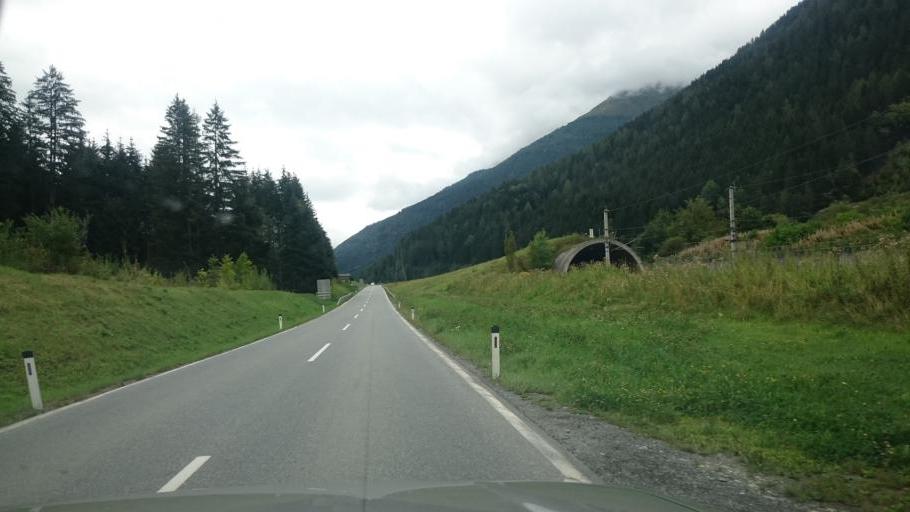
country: AT
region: Tyrol
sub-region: Politischer Bezirk Landeck
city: Sankt Anton am Arlberg
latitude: 47.1435
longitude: 10.3184
